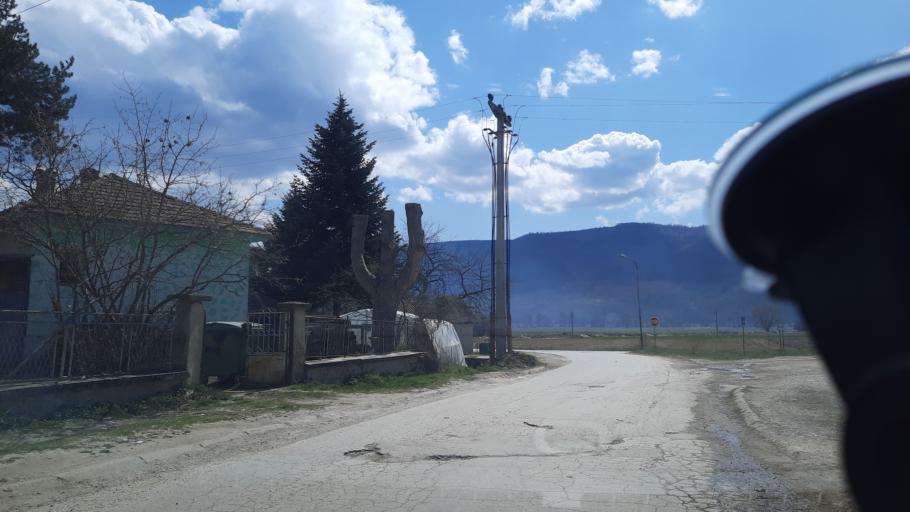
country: MK
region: Demir Hisar
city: Sopotnica
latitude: 41.2932
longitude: 21.1566
